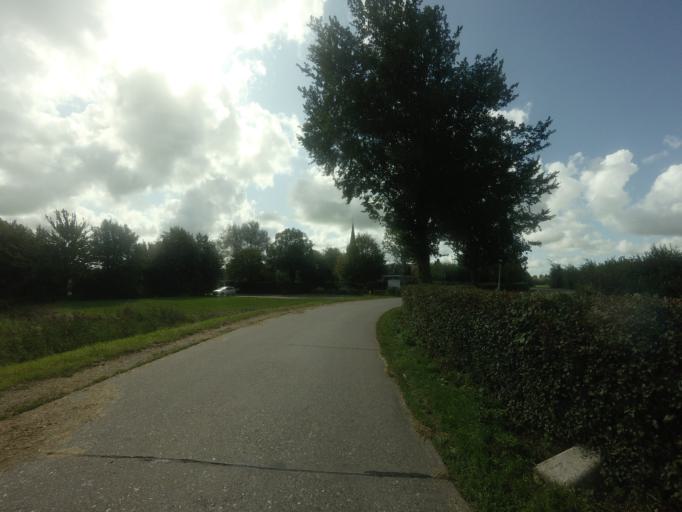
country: NL
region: Friesland
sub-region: Sudwest Fryslan
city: Scharnegoutum
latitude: 53.0773
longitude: 5.6386
